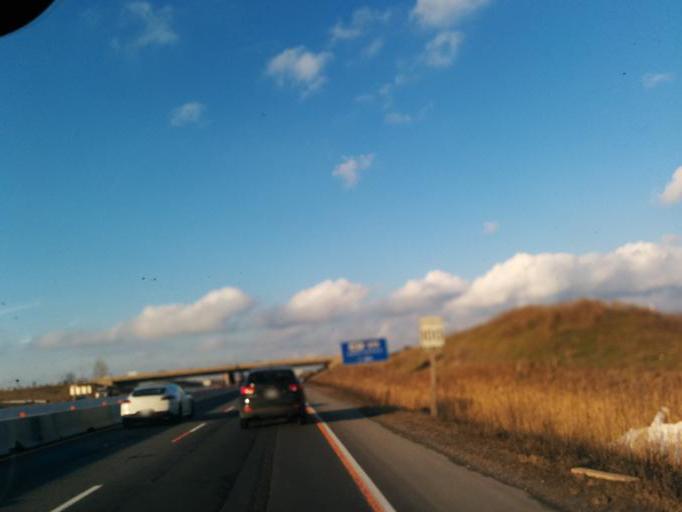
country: CA
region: Ontario
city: Etobicoke
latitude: 43.7320
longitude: -79.6266
